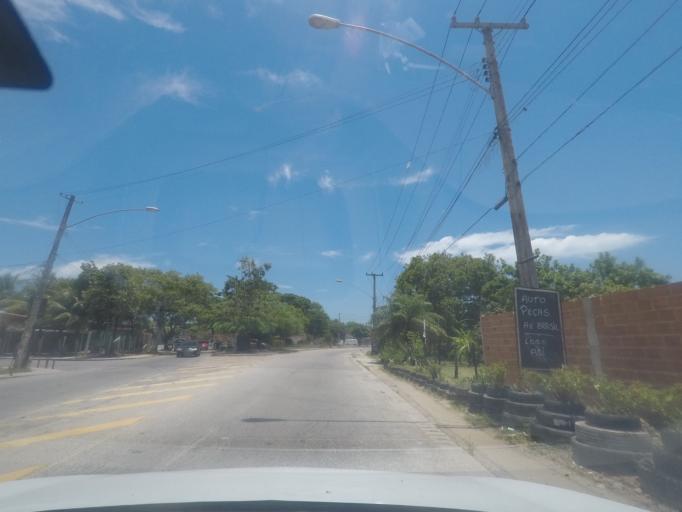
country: BR
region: Rio de Janeiro
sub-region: Itaguai
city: Itaguai
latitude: -22.9089
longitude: -43.6939
